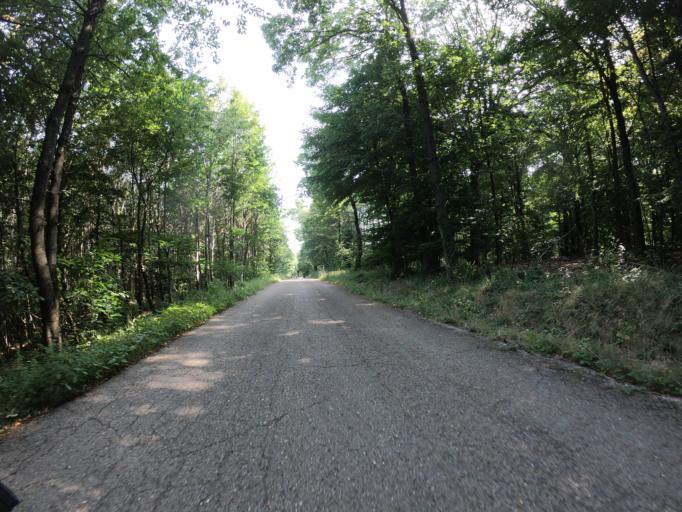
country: FR
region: Ile-de-France
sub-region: Departement de l'Essonne
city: Bievres
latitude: 48.7646
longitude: 2.2364
